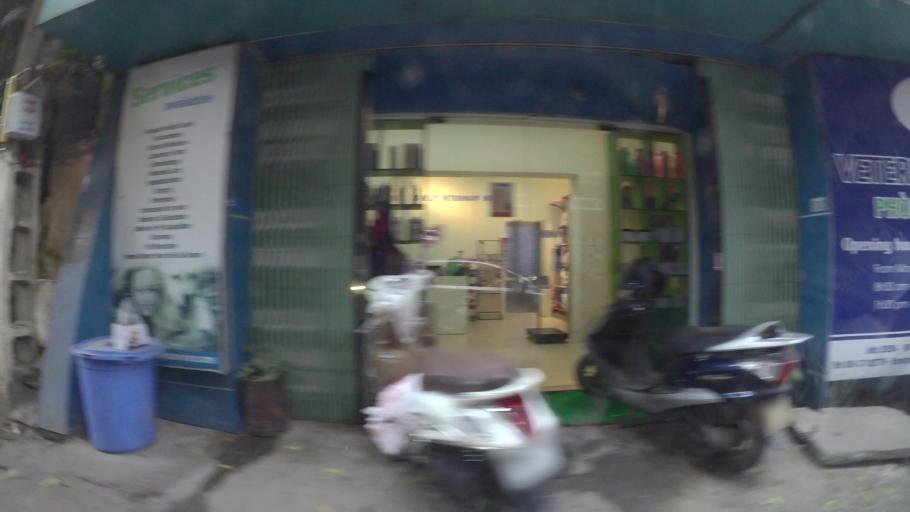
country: VN
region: Ha Noi
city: Tay Ho
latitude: 21.0679
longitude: 105.8225
